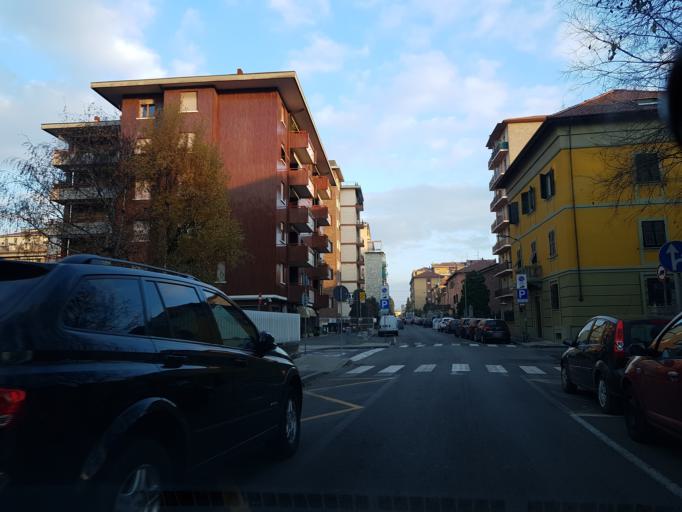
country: IT
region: Piedmont
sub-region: Provincia di Alessandria
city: Novi Ligure
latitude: 44.7647
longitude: 8.7912
